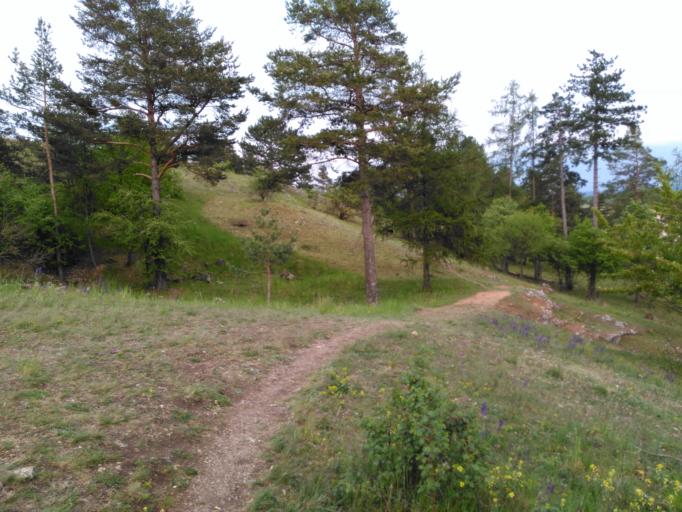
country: CZ
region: Central Bohemia
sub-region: Okres Beroun
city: Kraluv Dvur
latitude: 49.9163
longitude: 14.0649
